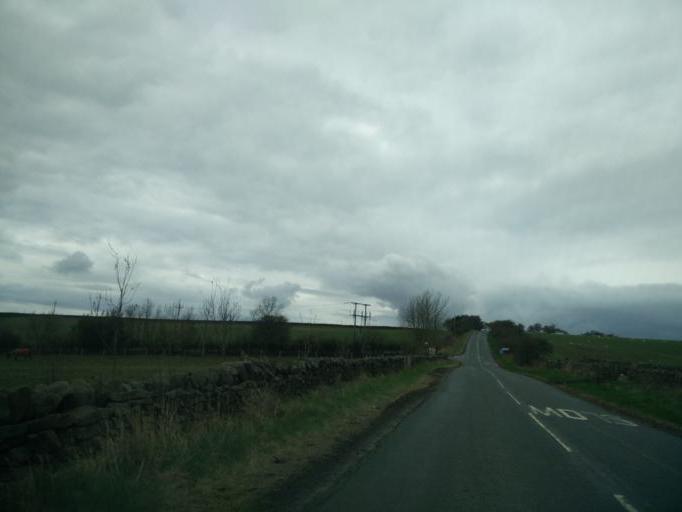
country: GB
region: England
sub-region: County Durham
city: Tow Law
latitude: 54.7384
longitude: -1.8469
